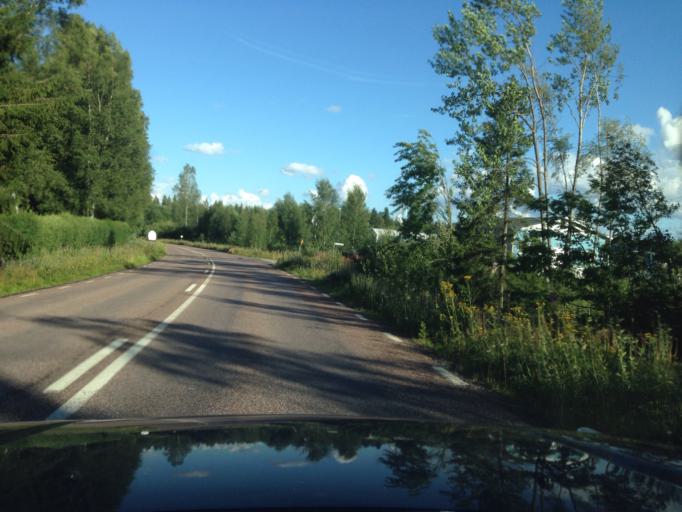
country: SE
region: Dalarna
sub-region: Ludvika Kommun
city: Ludvika
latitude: 60.1458
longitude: 15.1044
